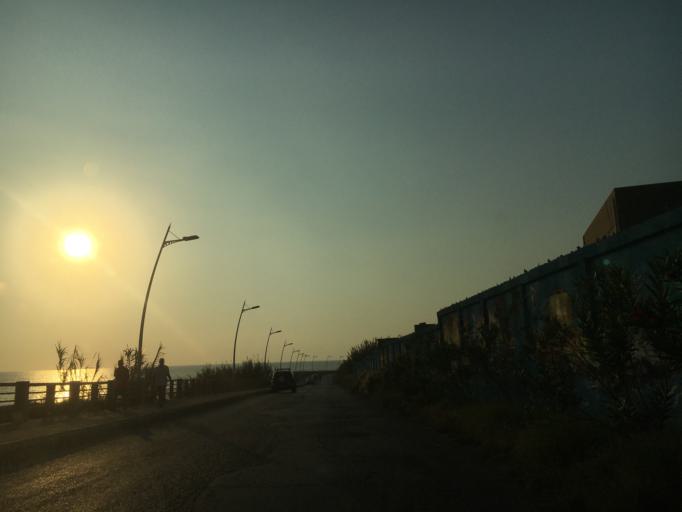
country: LB
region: Mont-Liban
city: Jbail
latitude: 34.1383
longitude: 35.6352
